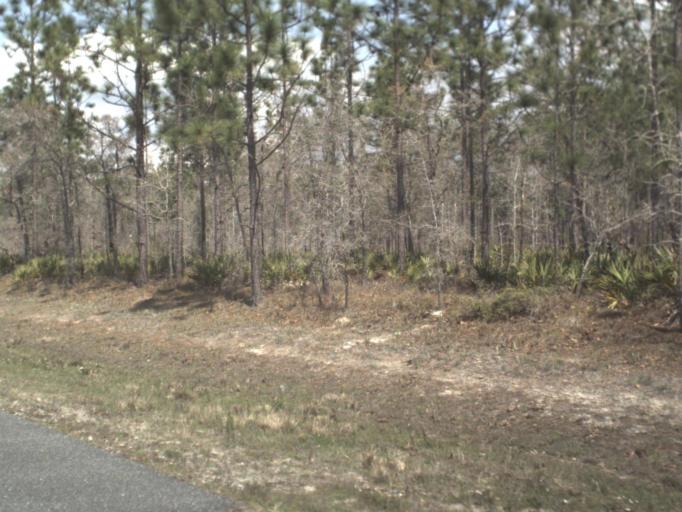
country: US
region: Florida
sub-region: Gulf County
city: Wewahitchka
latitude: 29.9967
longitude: -84.9772
